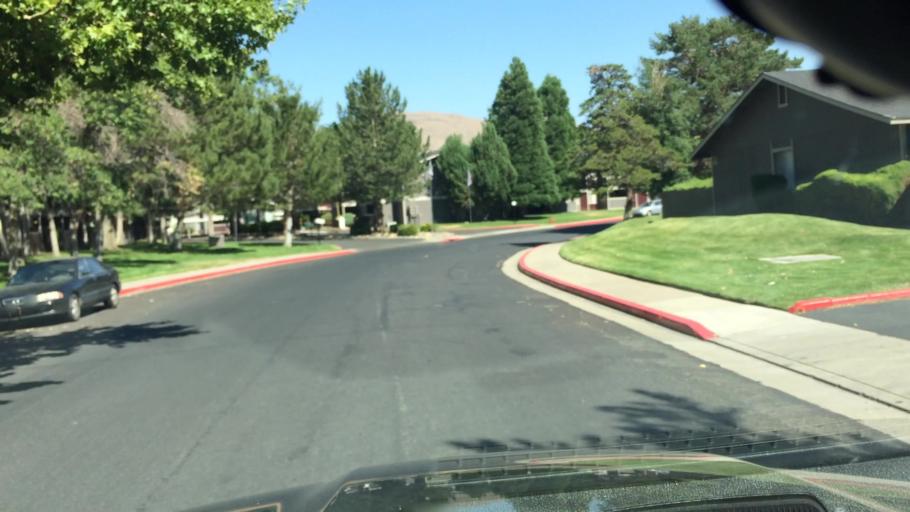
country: US
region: Nevada
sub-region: Washoe County
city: Sparks
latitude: 39.4826
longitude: -119.7476
